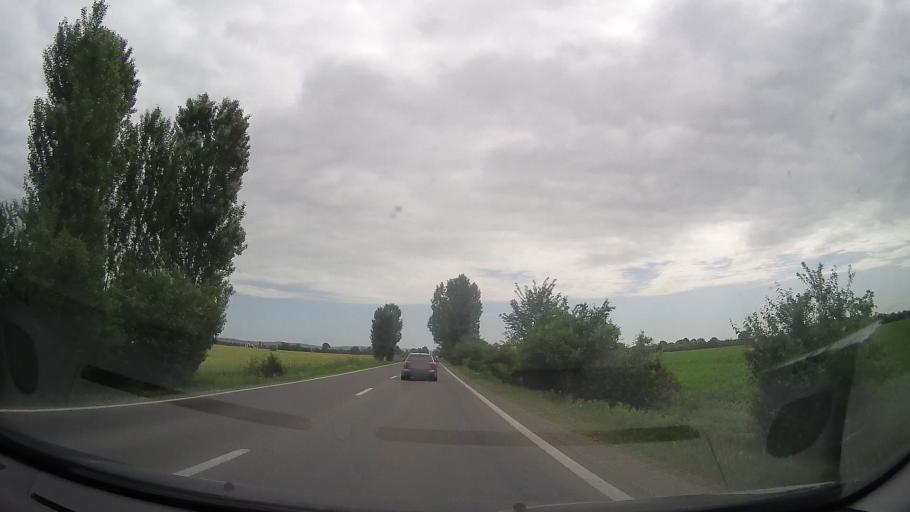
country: RO
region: Prahova
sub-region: Comuna Barcanesti
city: Barcanesti
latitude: 44.8977
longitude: 26.0589
